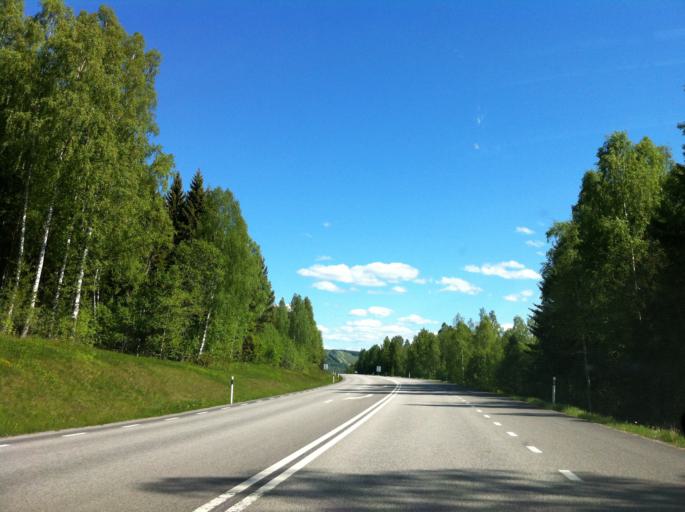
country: SE
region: Dalarna
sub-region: Rattviks Kommun
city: Raettvik
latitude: 60.9031
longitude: 15.0734
